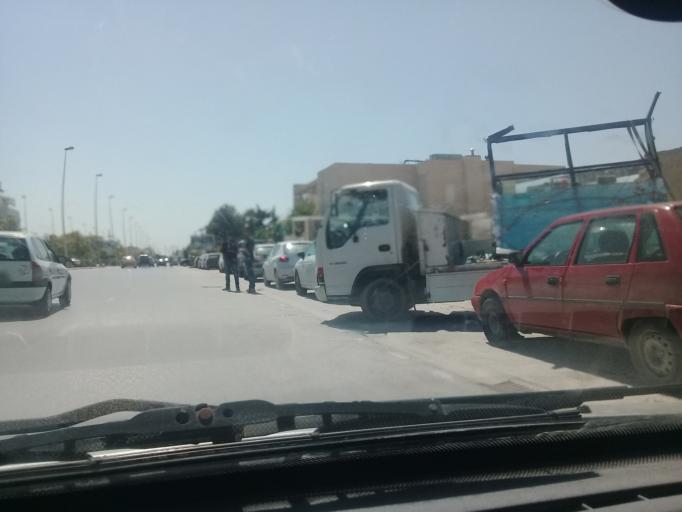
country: TN
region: Ariana
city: Ariana
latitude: 36.8365
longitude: 10.2430
